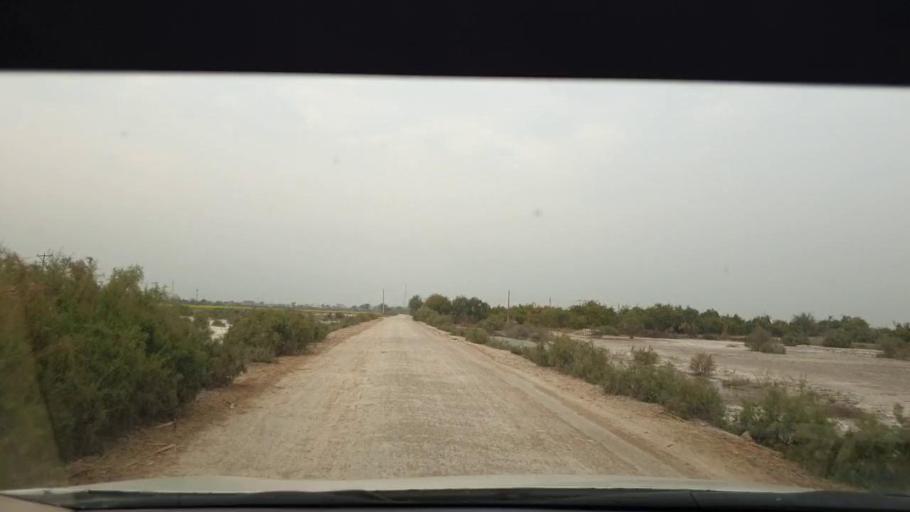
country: PK
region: Sindh
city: Sinjhoro
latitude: 25.9251
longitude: 68.7548
